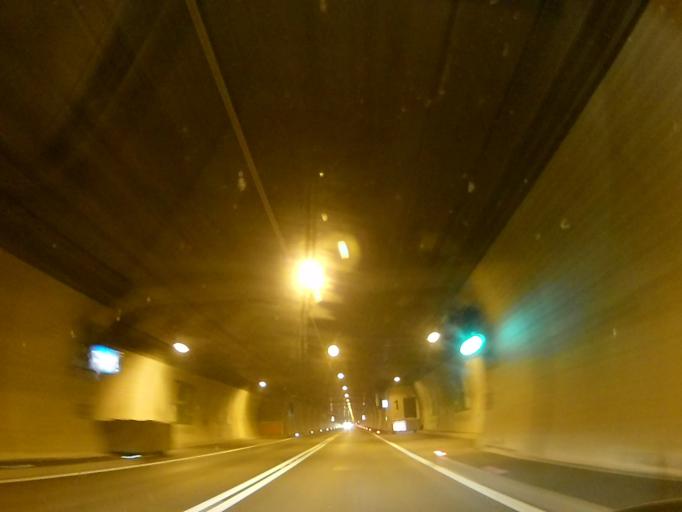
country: AT
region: Tyrol
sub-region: Politischer Bezirk Landeck
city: Zams
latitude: 47.1630
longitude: 10.6113
